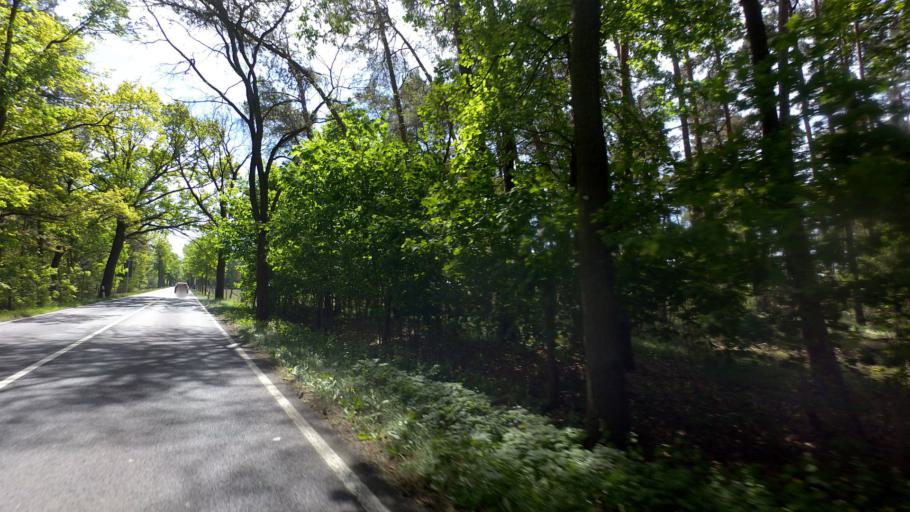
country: DE
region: Brandenburg
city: Luckenwalde
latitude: 52.1222
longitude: 13.1337
